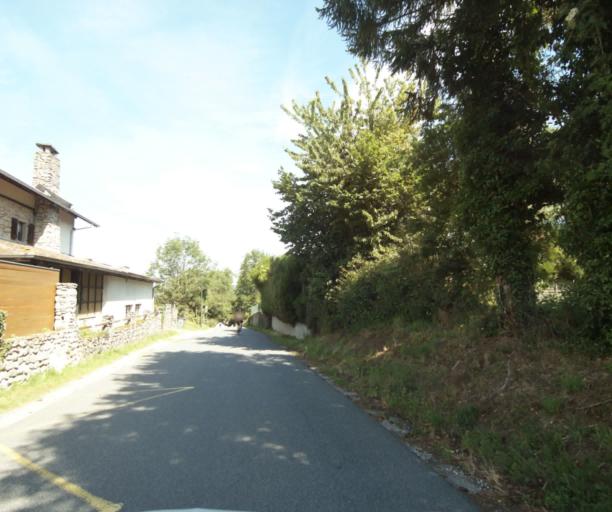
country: FR
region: Rhone-Alpes
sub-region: Departement de la Haute-Savoie
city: Anthy-sur-Leman
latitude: 46.3495
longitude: 6.4074
